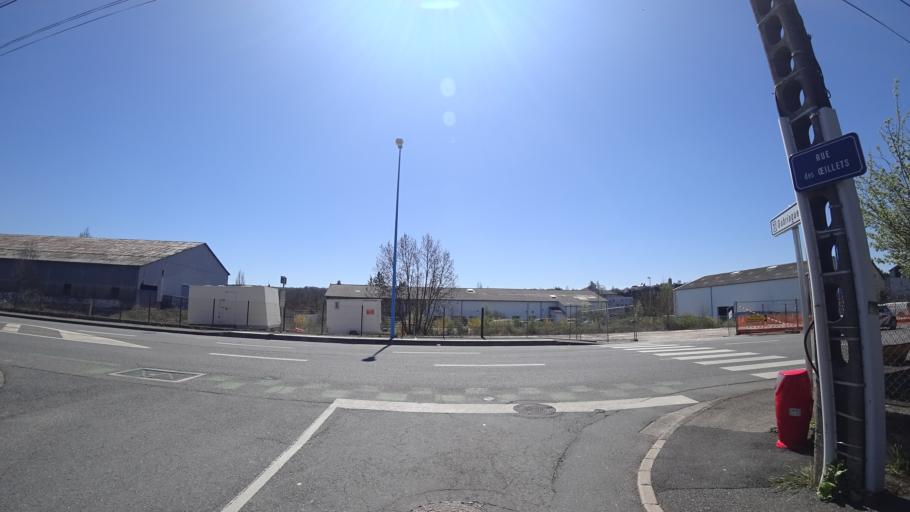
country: FR
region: Midi-Pyrenees
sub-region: Departement de l'Aveyron
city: Rodez
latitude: 44.3622
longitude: 2.5933
